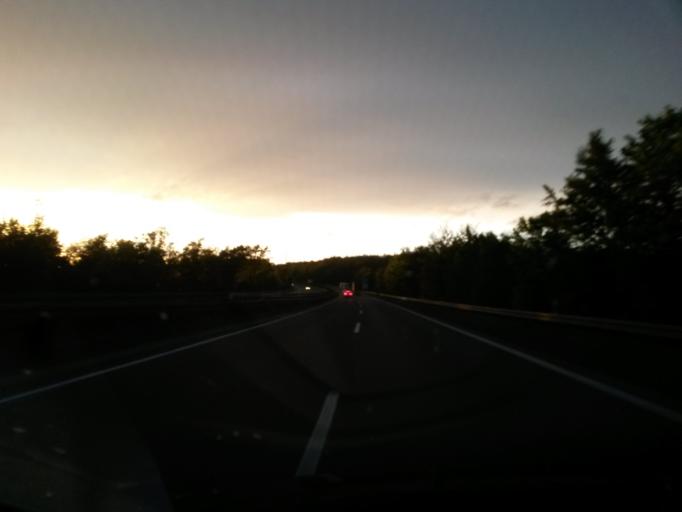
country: DE
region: Hesse
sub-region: Regierungsbezirk Kassel
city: Burghaun
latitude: 50.7023
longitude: 9.6783
